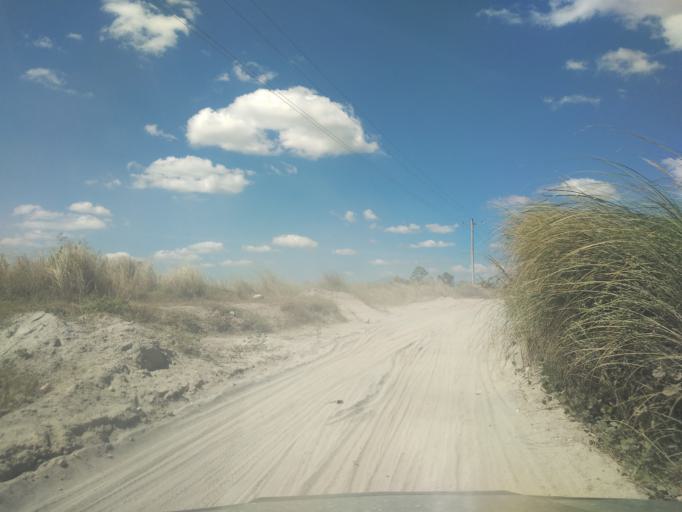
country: PH
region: Central Luzon
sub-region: Province of Pampanga
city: Balas
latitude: 15.0604
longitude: 120.5940
